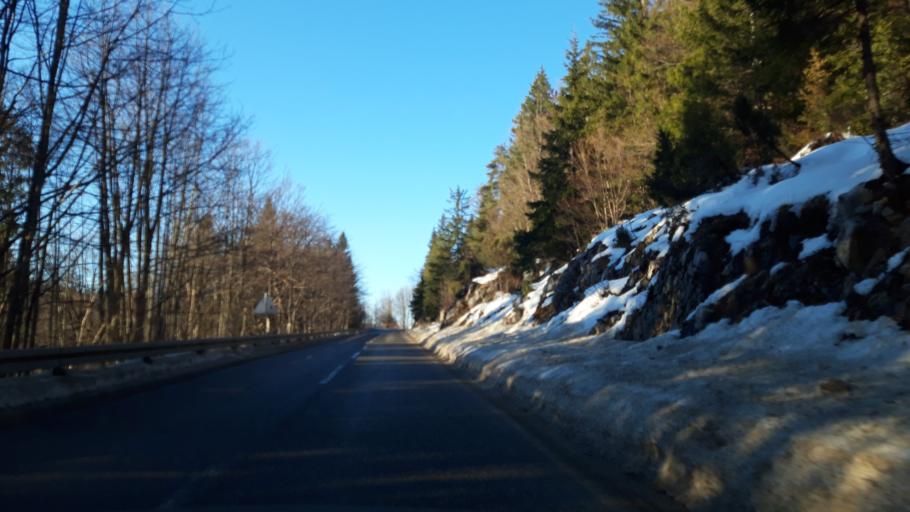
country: BA
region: Republika Srpska
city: Vlasenica
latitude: 44.1391
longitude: 18.9512
